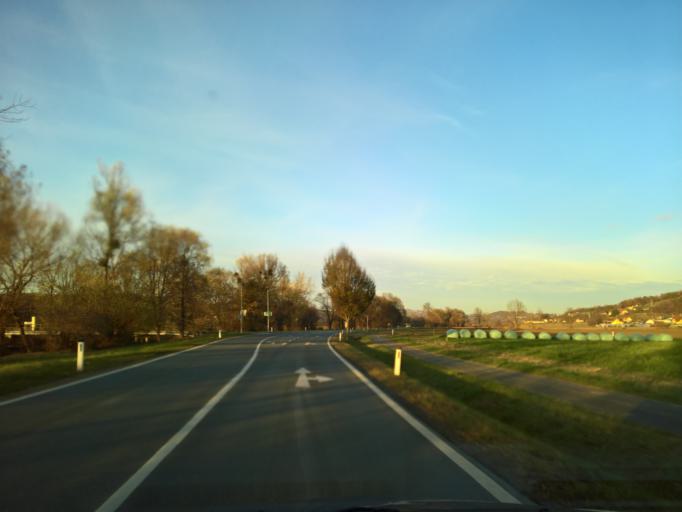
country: AT
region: Styria
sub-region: Politischer Bezirk Leibnitz
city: Sankt Johann im Saggautal
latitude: 46.7077
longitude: 15.3969
